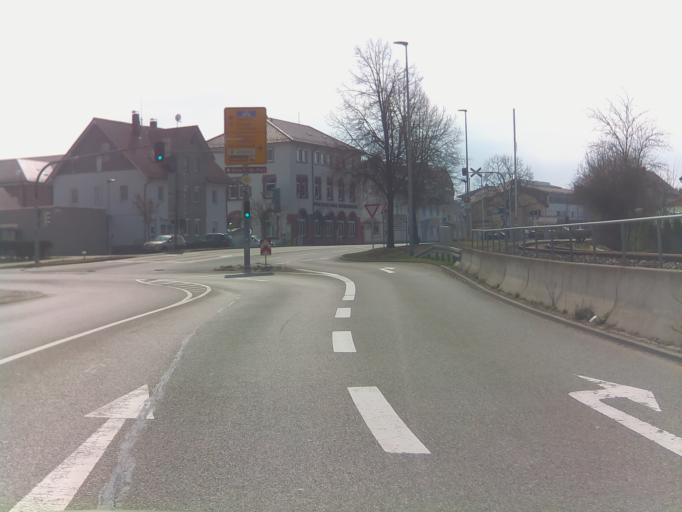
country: DE
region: Baden-Wuerttemberg
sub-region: Tuebingen Region
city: Munsingen
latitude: 48.4120
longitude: 9.4910
